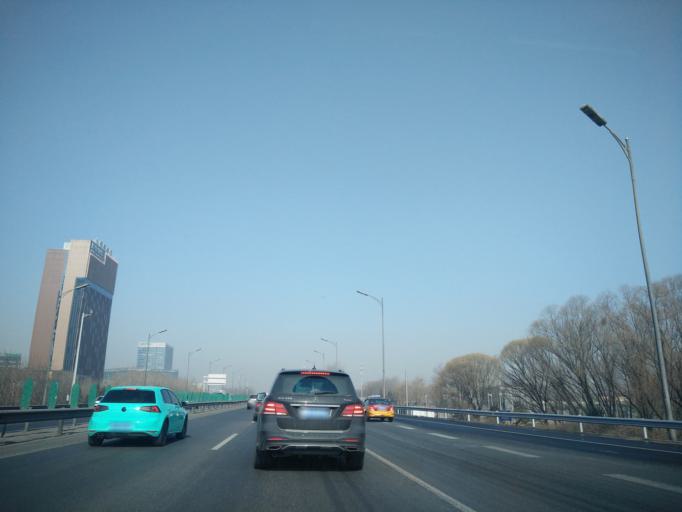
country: CN
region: Beijing
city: Wangjing
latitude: 40.0036
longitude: 116.4885
